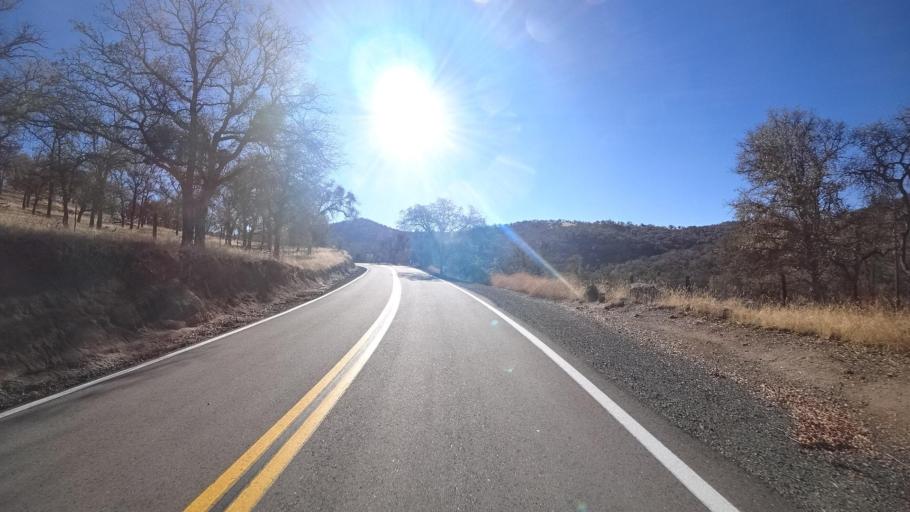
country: US
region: California
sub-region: Kern County
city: Alta Sierra
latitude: 35.7068
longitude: -118.7689
